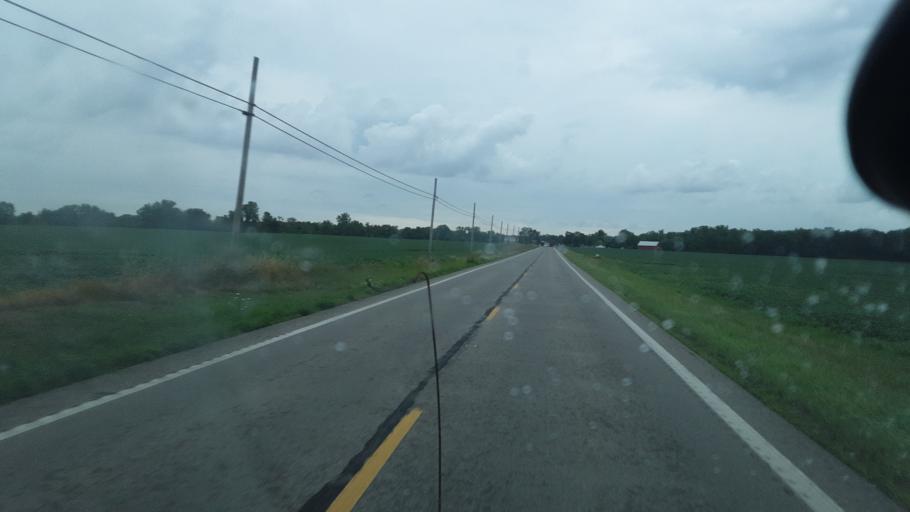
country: US
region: Ohio
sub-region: Williams County
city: Bryan
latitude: 41.4353
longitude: -84.6037
